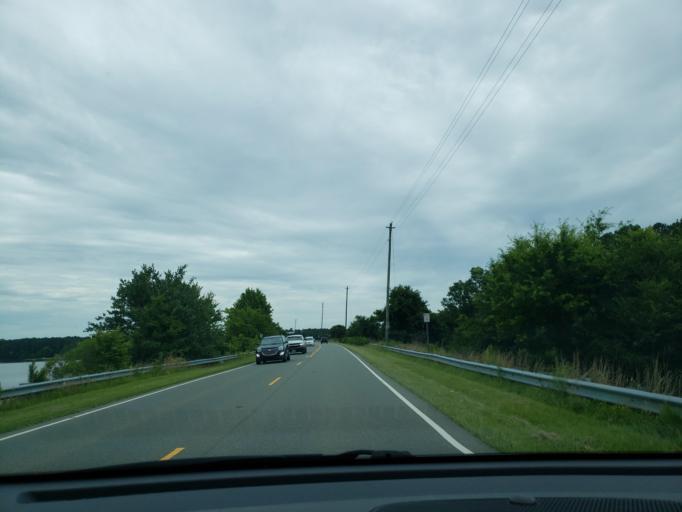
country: US
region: North Carolina
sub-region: Chatham County
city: Fearrington Village
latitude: 35.7917
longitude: -79.0102
